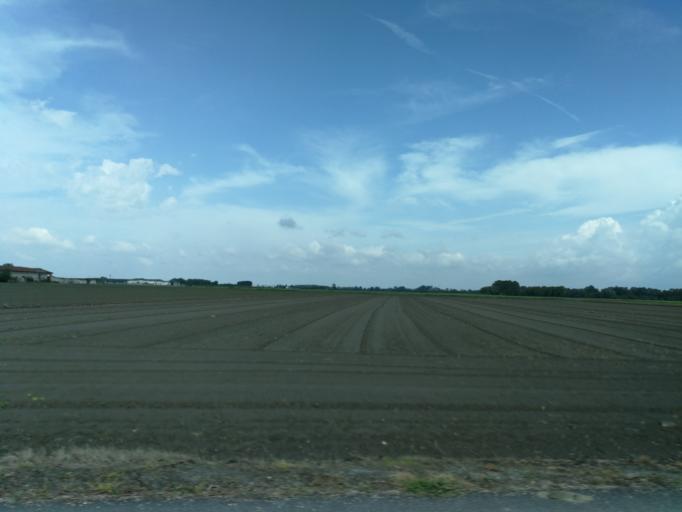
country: IT
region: Piedmont
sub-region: Provincia di Torino
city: Pancalieri
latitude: 44.8251
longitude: 7.5874
